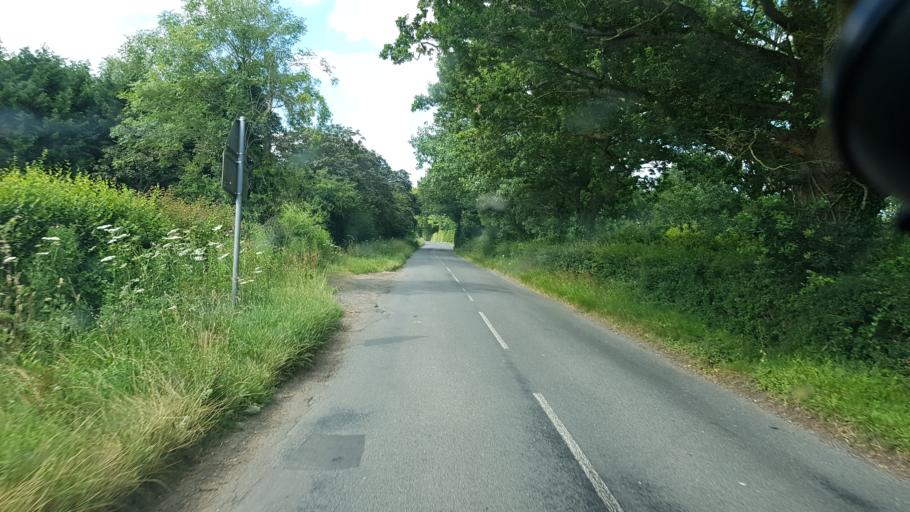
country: GB
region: England
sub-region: West Sussex
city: Rudgwick
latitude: 51.0653
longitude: -0.4472
